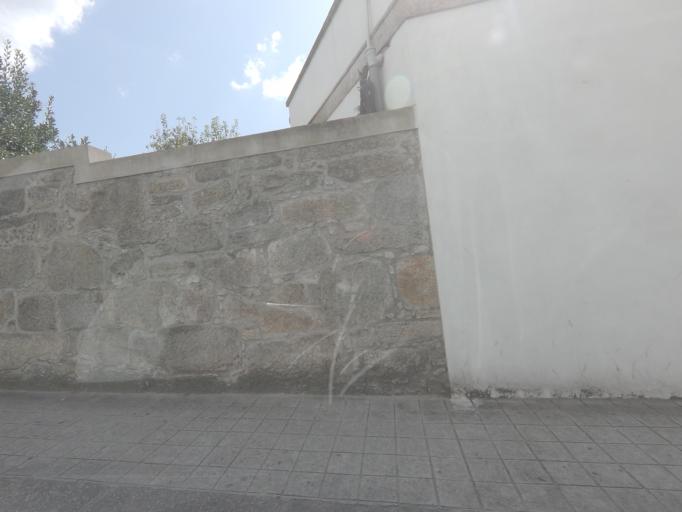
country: PT
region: Porto
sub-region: Porto
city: Porto
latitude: 41.1634
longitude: -8.6254
